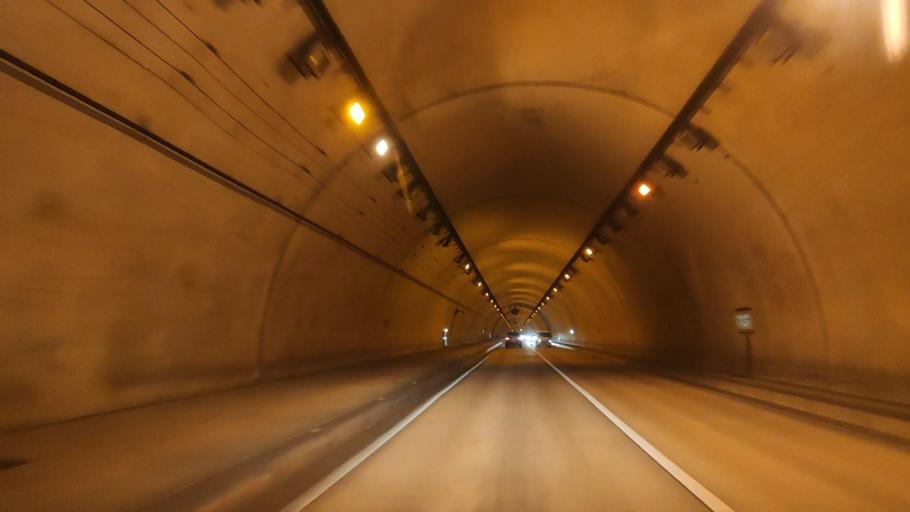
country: JP
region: Ehime
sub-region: Shikoku-chuo Shi
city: Matsuyama
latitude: 33.8770
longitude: 132.7137
